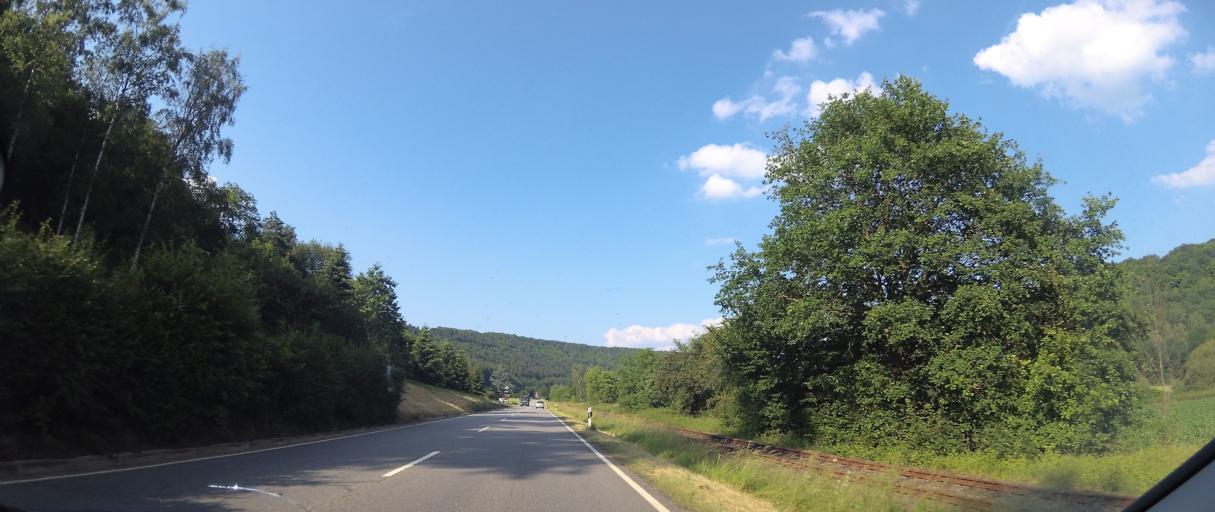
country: DE
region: Rheinland-Pfalz
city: Medard
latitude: 49.6723
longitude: 7.6197
